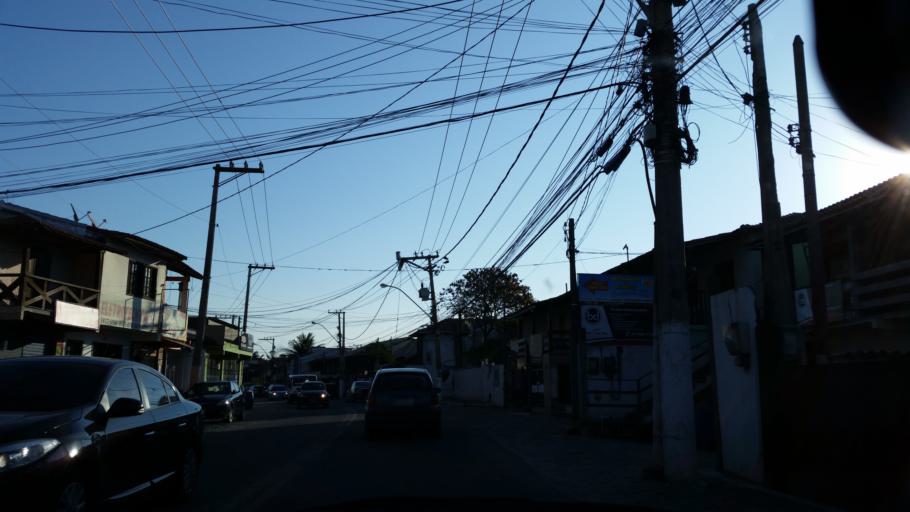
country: BR
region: Rio de Janeiro
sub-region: Armacao De Buzios
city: Armacao de Buzios
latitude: -22.7705
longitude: -41.9115
